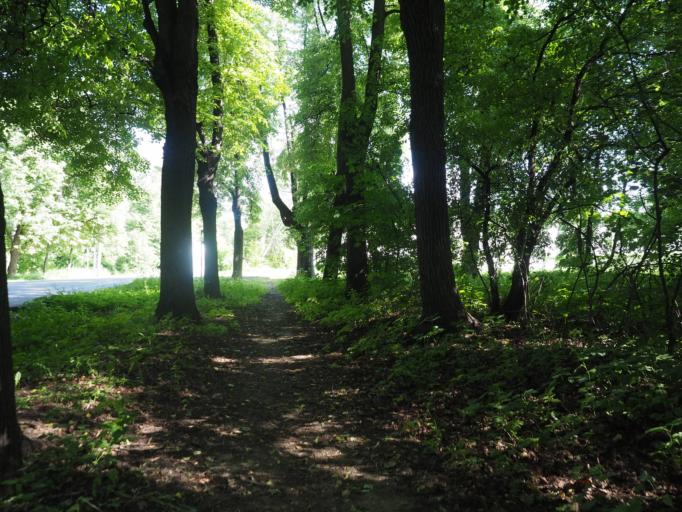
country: RU
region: Moskovskaya
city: Bogorodskoye
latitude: 55.7796
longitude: 37.7484
